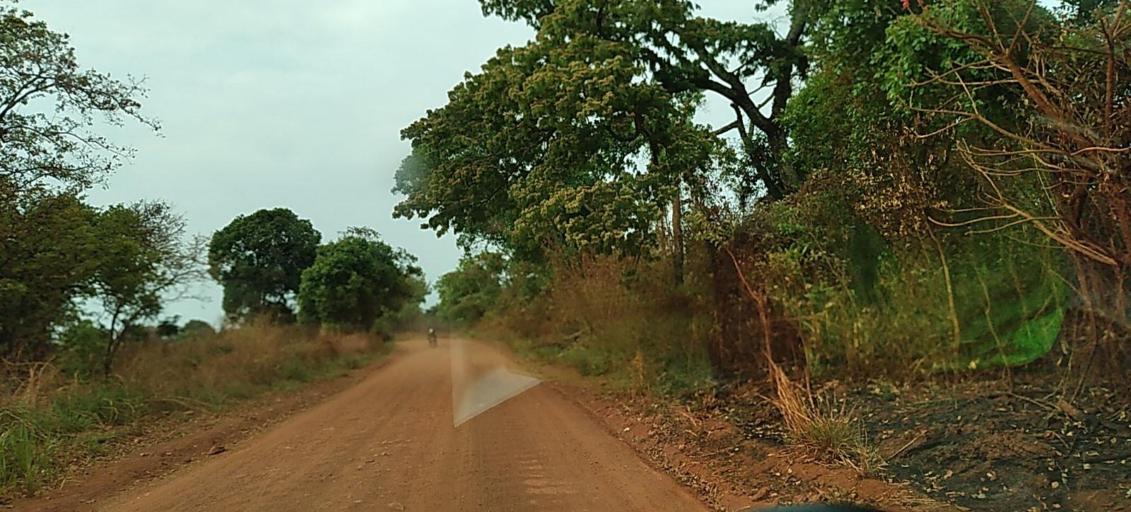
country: ZM
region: North-Western
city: Solwezi
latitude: -12.2255
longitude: 26.5106
